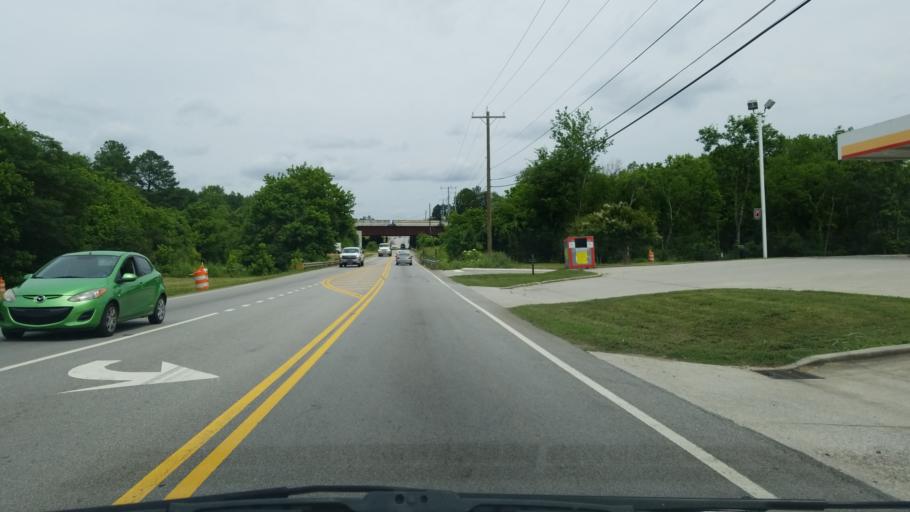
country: US
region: Tennessee
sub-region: Hamilton County
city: Harrison
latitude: 35.0733
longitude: -85.1623
